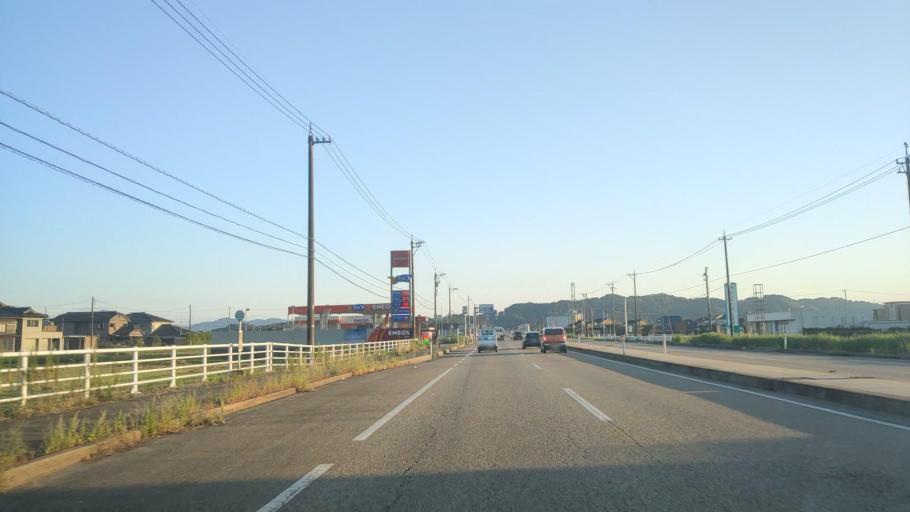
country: JP
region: Toyama
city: Himi
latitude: 36.8713
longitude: 136.9753
